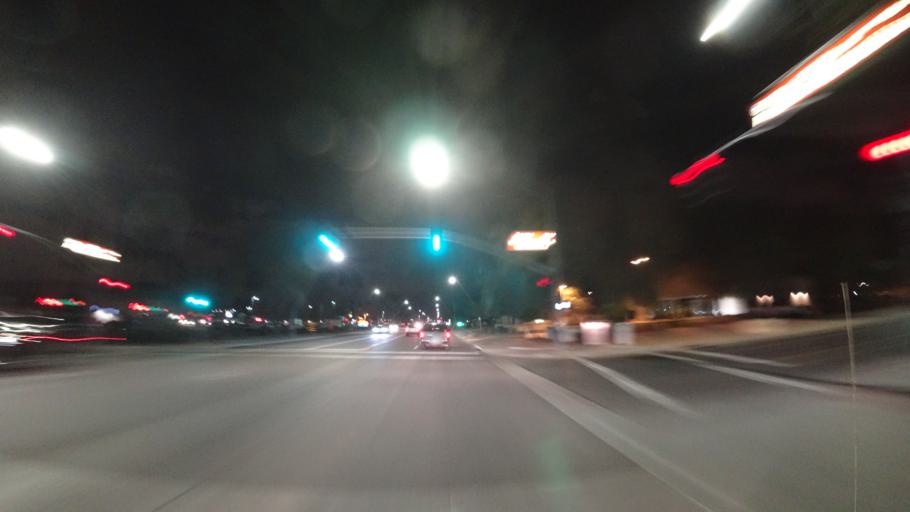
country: US
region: Arizona
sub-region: Maricopa County
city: Chandler
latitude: 33.3131
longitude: -111.8591
